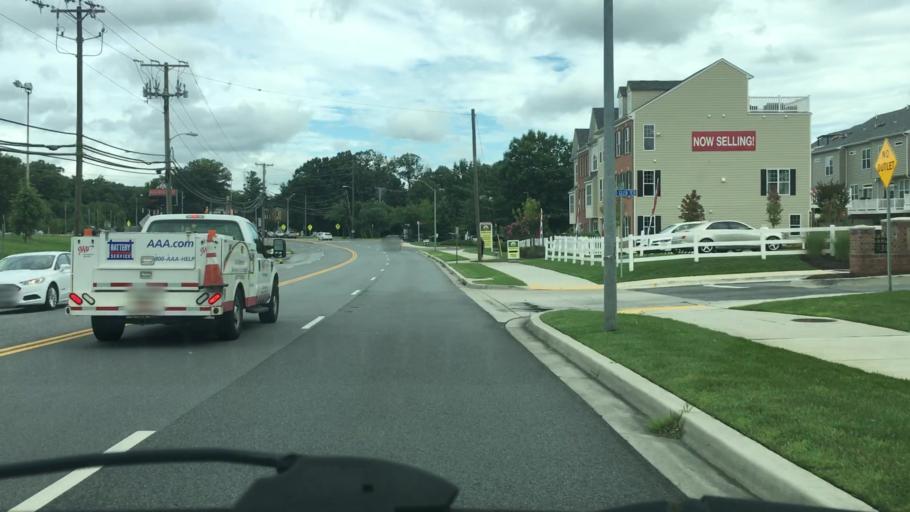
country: US
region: Maryland
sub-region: Prince George's County
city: Glenn Dale
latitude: 38.9888
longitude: -76.8365
